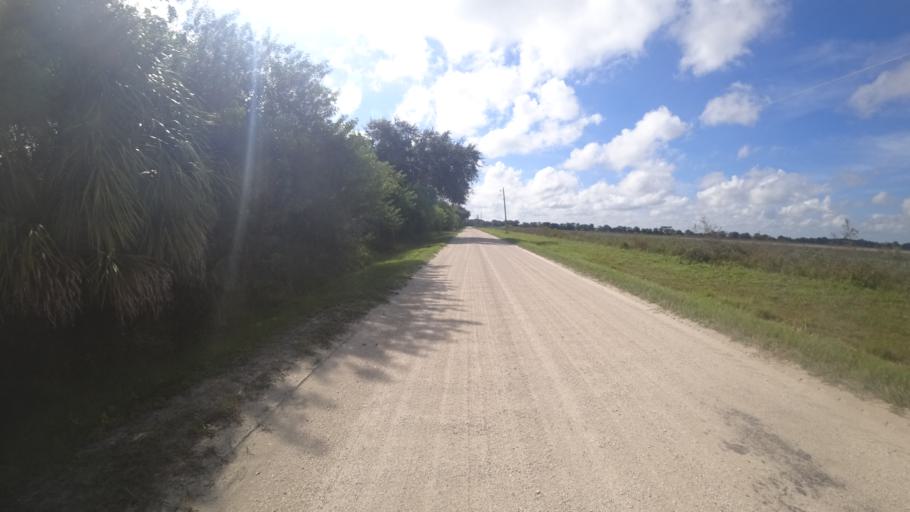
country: US
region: Florida
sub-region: Hillsborough County
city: Ruskin
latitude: 27.6364
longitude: -82.4171
